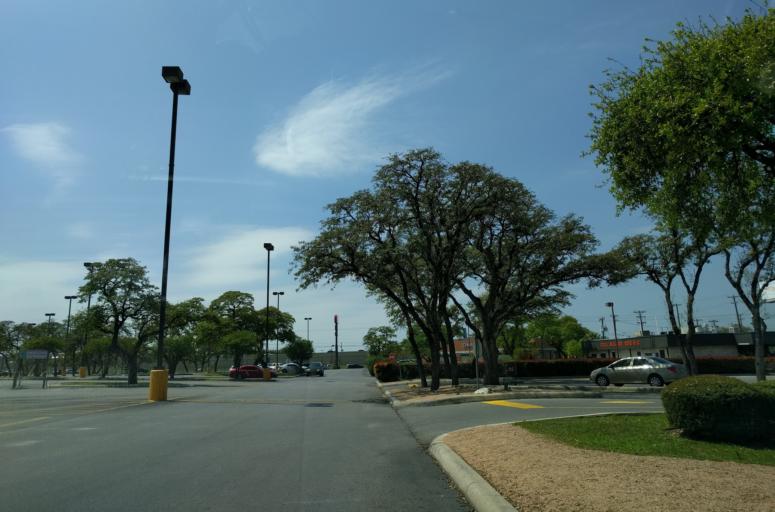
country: US
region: Texas
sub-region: Bexar County
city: Shavano Park
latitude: 29.5631
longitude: -98.5882
